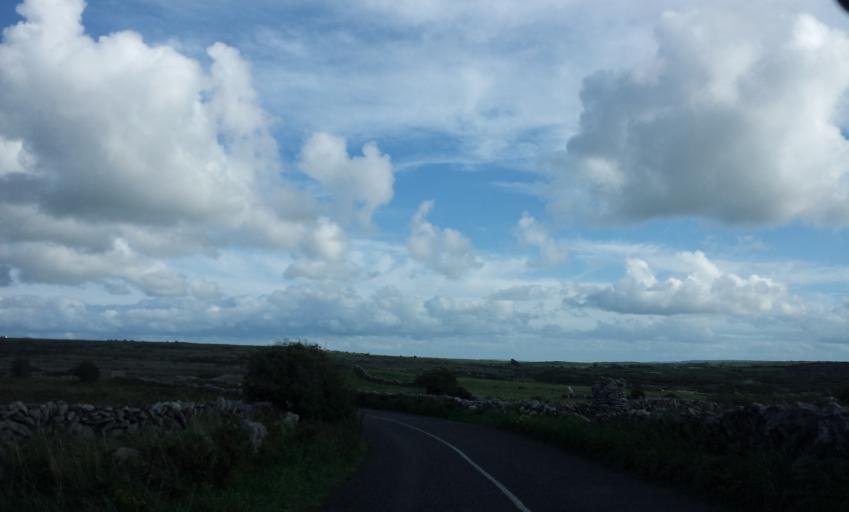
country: IE
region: Connaught
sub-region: County Galway
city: Bearna
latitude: 53.0600
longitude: -9.1486
